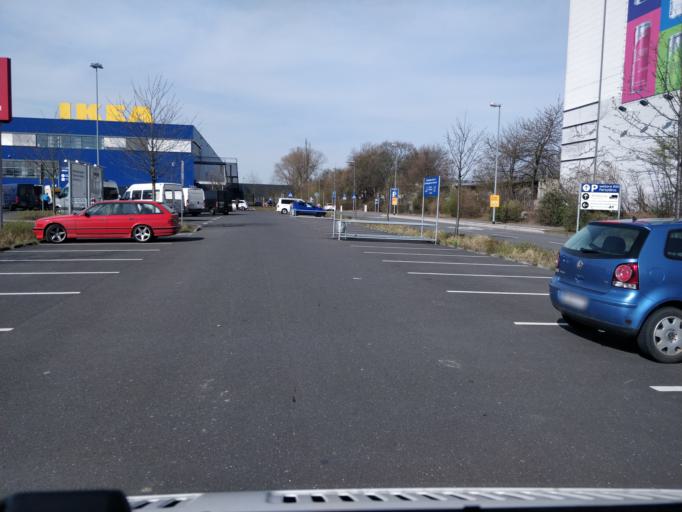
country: DE
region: North Rhine-Westphalia
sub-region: Regierungsbezirk Koln
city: Mengenich
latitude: 50.9858
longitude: 6.8995
